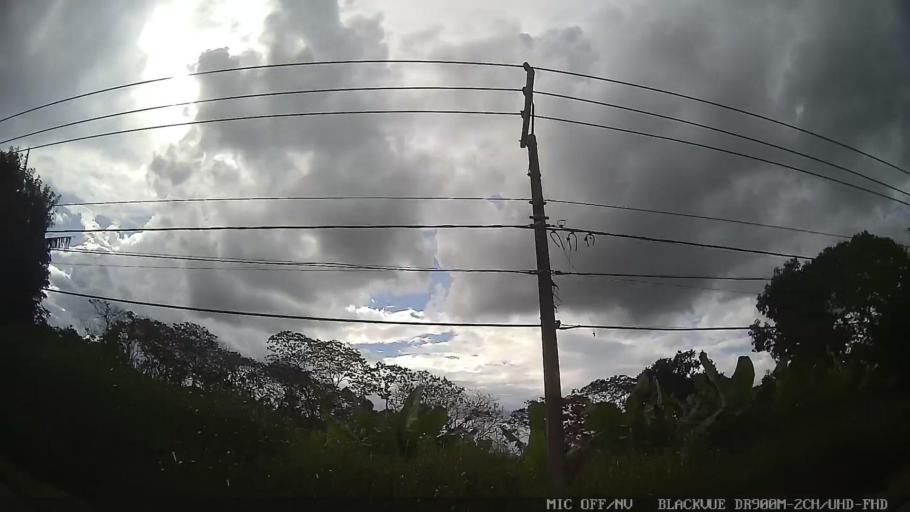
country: BR
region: Sao Paulo
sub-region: Mogi das Cruzes
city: Mogi das Cruzes
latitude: -23.5572
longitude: -46.1295
